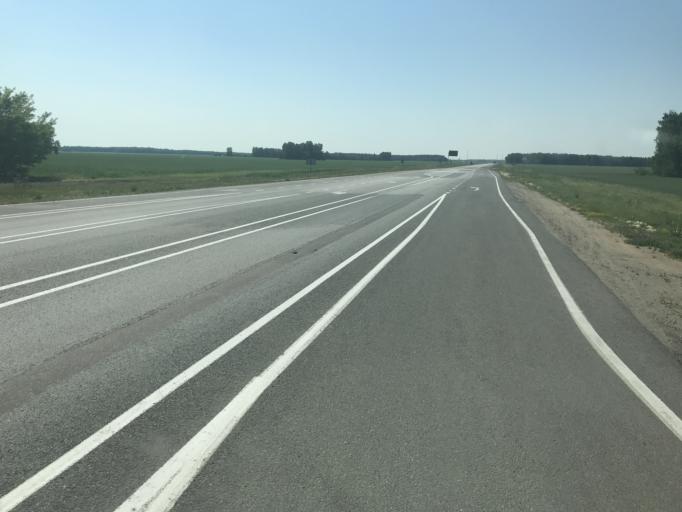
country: KZ
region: Soltustik Qazaqstan
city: Bishkul
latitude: 54.6636
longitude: 69.1478
